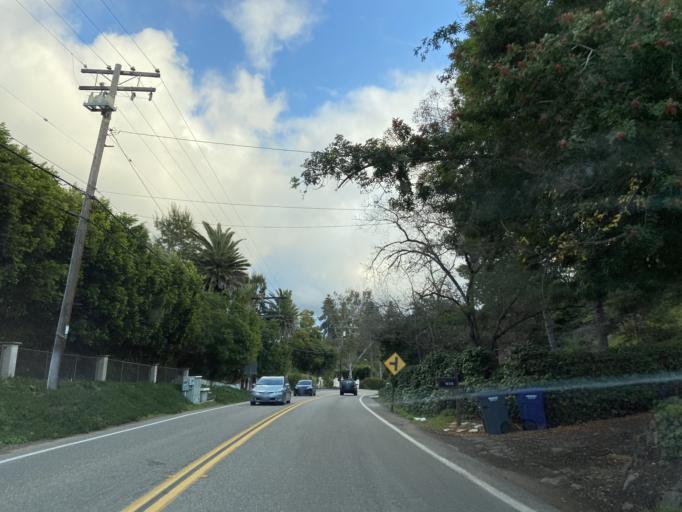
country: US
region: California
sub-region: San Diego County
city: Casa de Oro-Mount Helix
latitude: 32.7708
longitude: -116.9757
